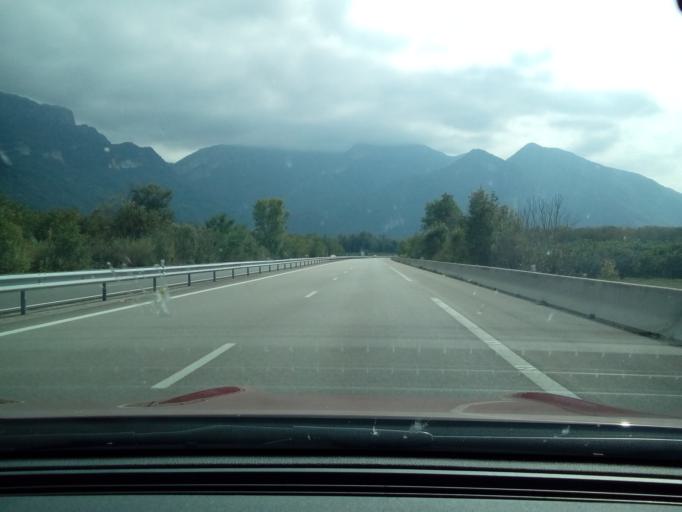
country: FR
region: Rhone-Alpes
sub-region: Departement de l'Isere
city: Tullins
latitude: 45.2262
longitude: 5.4813
